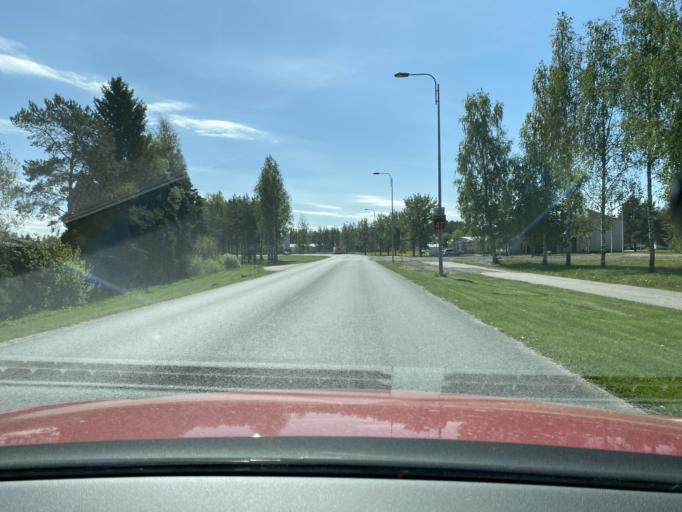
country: FI
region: Satakunta
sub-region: Rauma
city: Eura
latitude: 61.1279
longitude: 22.1455
